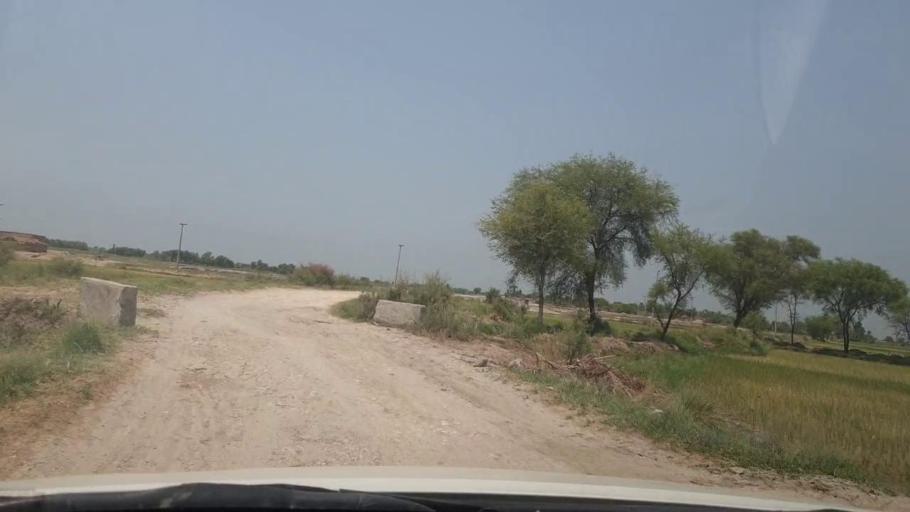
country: PK
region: Sindh
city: Rustam jo Goth
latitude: 28.0377
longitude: 68.7550
